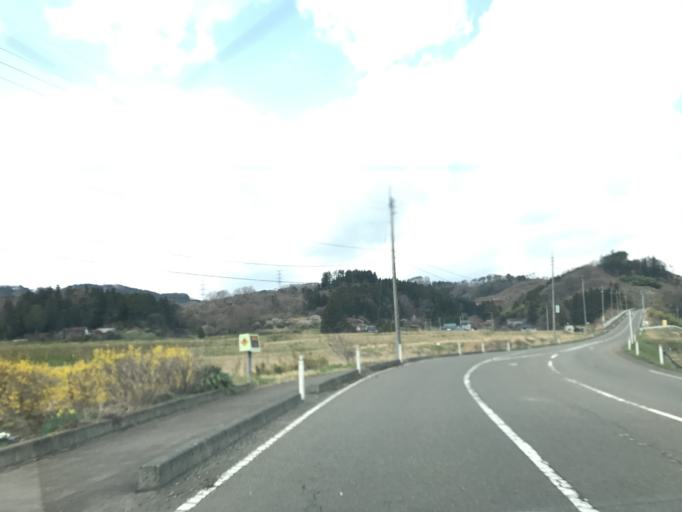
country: JP
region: Miyagi
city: Shiroishi
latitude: 38.0119
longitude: 140.5848
